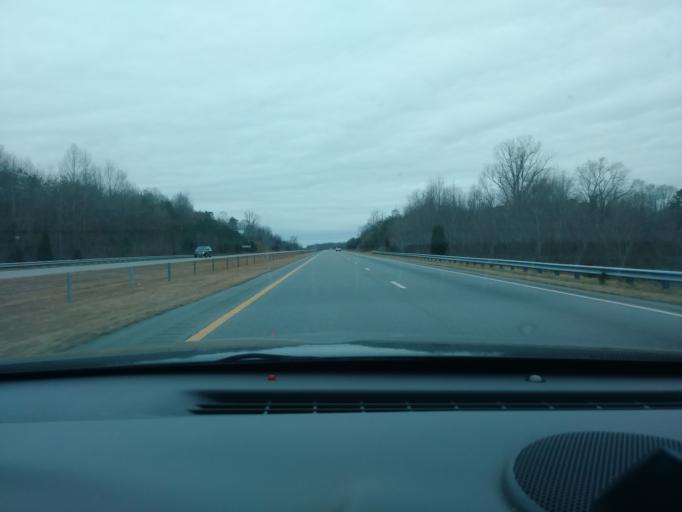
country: US
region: North Carolina
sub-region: Yadkin County
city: Yadkinville
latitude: 36.1197
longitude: -80.6838
